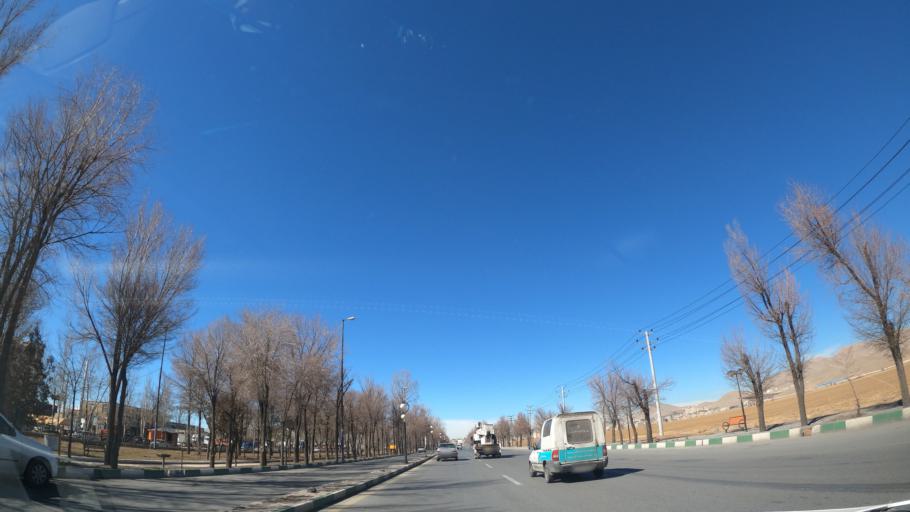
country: IR
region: Chahar Mahall va Bakhtiari
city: Shahrekord
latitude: 32.3081
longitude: 50.8998
